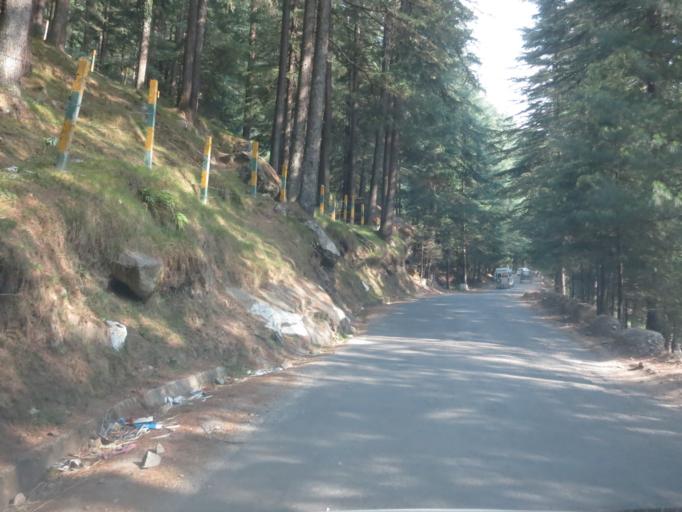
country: IN
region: Himachal Pradesh
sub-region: Kulu
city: Nagar
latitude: 32.1663
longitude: 77.1931
